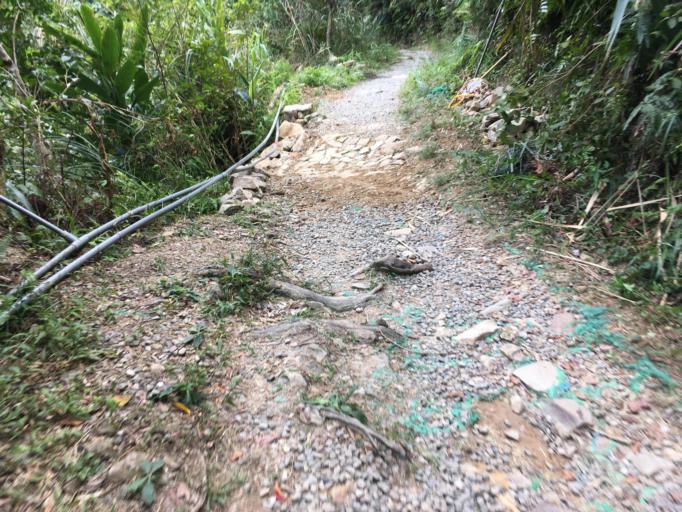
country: TW
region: Taiwan
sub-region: Yilan
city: Yilan
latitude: 24.8478
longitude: 121.7754
